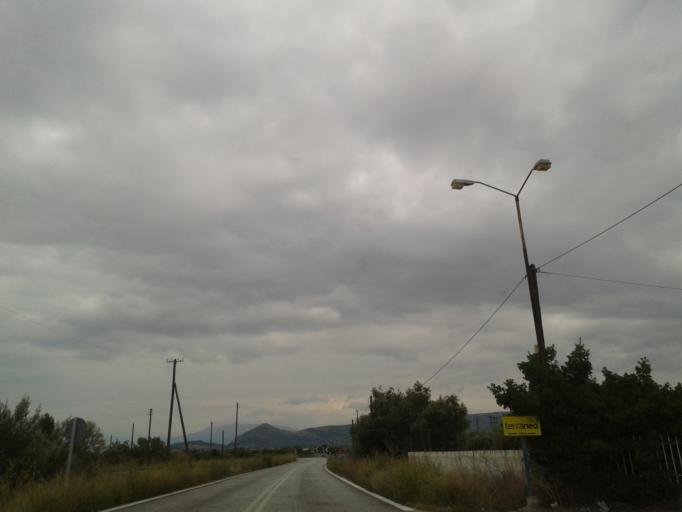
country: GR
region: Peloponnese
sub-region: Nomos Argolidos
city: Koutsopodi
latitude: 37.7036
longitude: 22.7236
